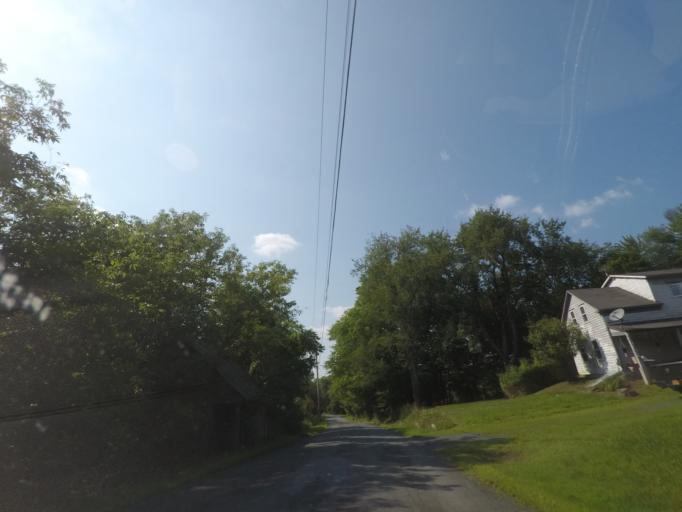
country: US
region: New York
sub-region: Rensselaer County
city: Nassau
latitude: 42.5345
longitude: -73.5724
